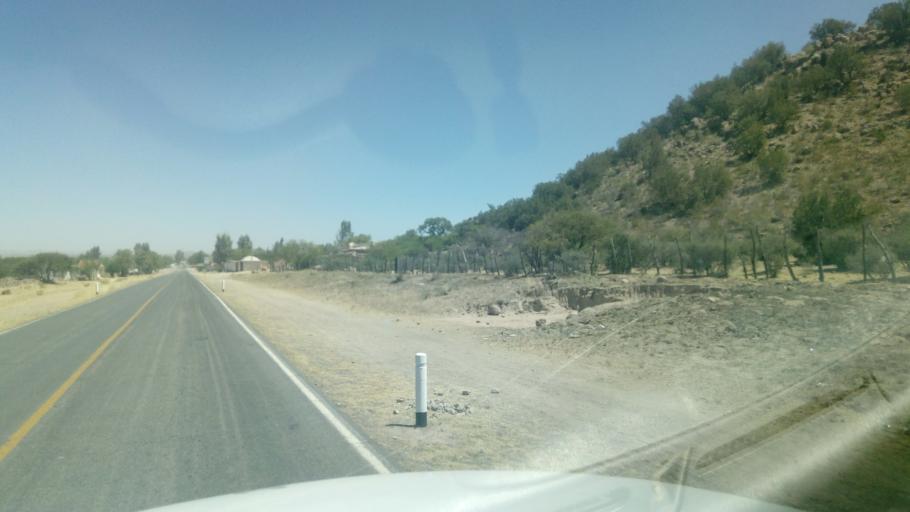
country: MX
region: Durango
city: Victoria de Durango
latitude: 24.1638
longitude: -104.7034
